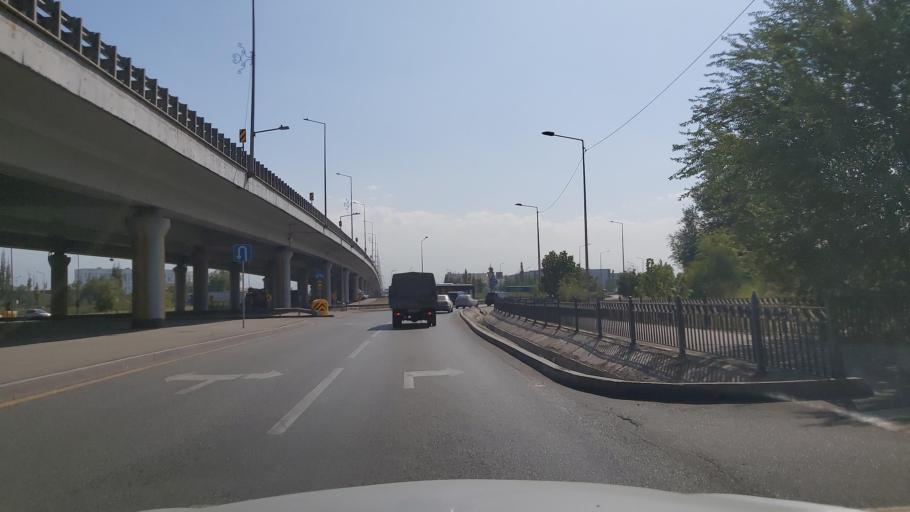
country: KZ
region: Almaty Qalasy
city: Almaty
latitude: 43.3046
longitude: 76.8962
